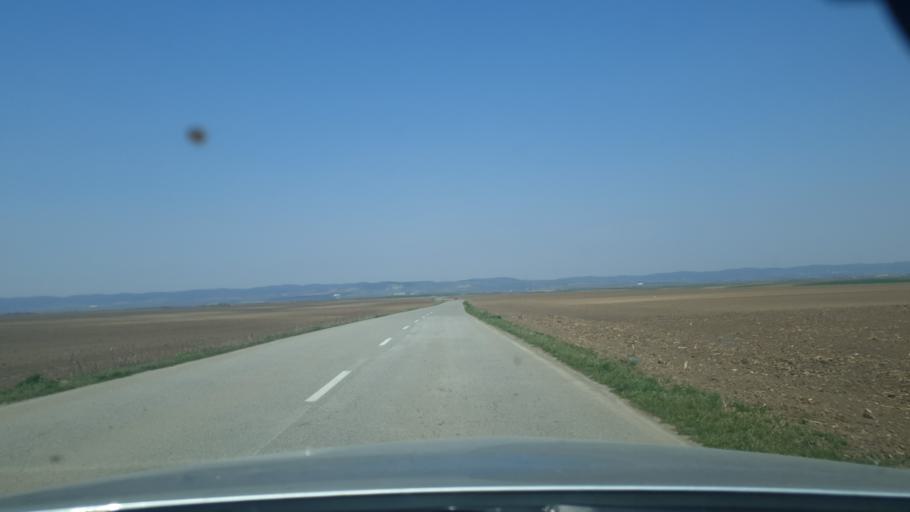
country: RS
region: Autonomna Pokrajina Vojvodina
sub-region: Sremski Okrug
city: Ruma
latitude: 45.0294
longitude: 19.7623
